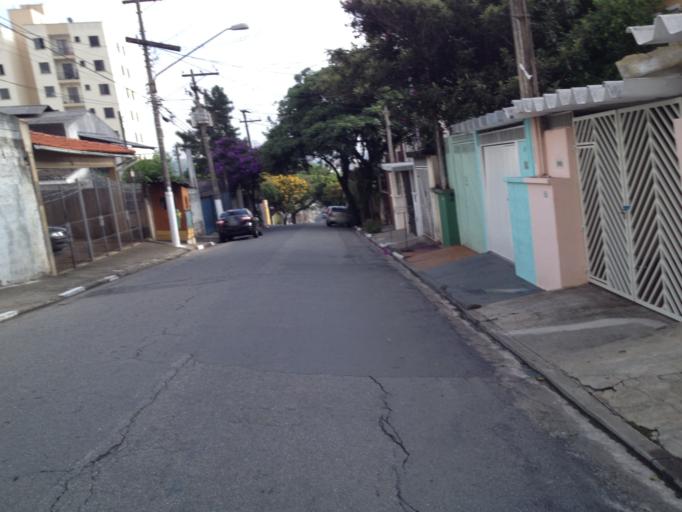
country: BR
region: Sao Paulo
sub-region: Taboao Da Serra
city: Taboao da Serra
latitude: -23.6472
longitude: -46.7405
